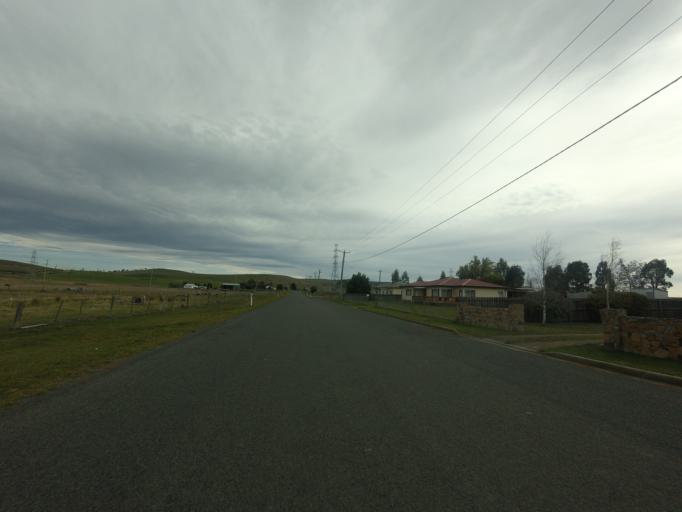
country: AU
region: Tasmania
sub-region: Derwent Valley
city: New Norfolk
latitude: -42.3838
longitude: 146.9896
